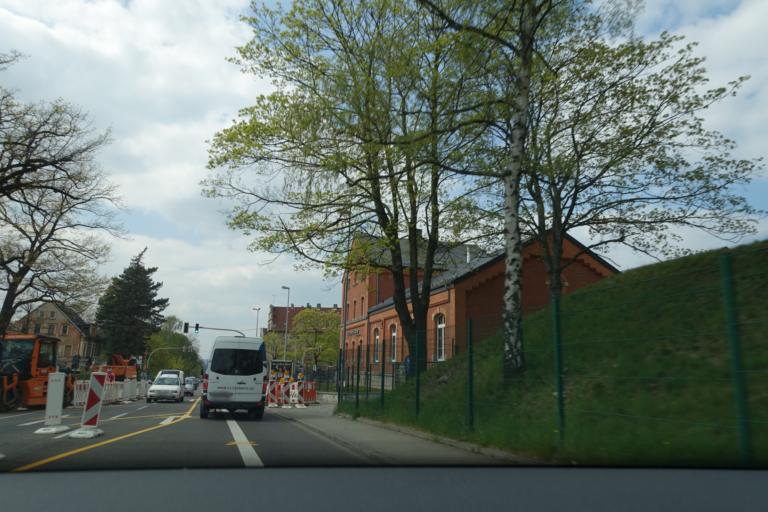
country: DE
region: Saxony
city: Chemnitz
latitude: 50.8186
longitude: 12.9450
